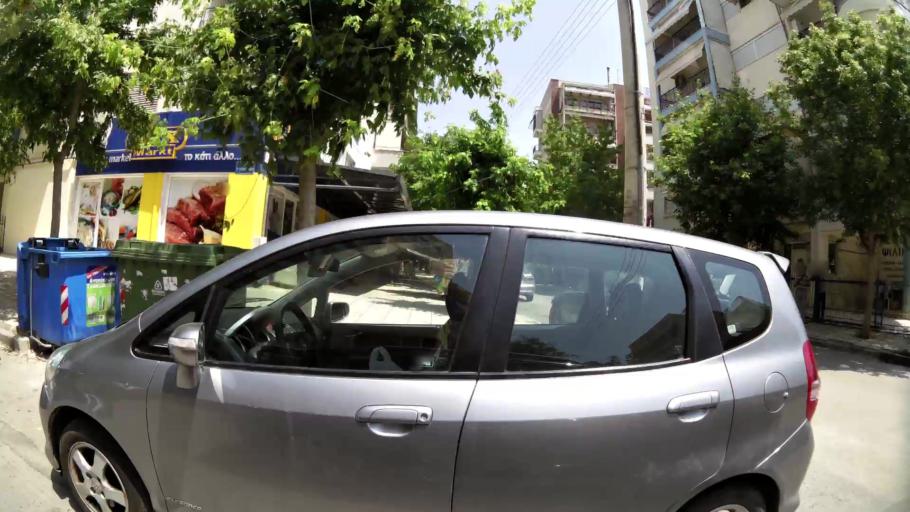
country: GR
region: Central Macedonia
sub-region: Nomos Thessalonikis
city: Menemeni
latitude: 40.6681
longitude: 22.8914
